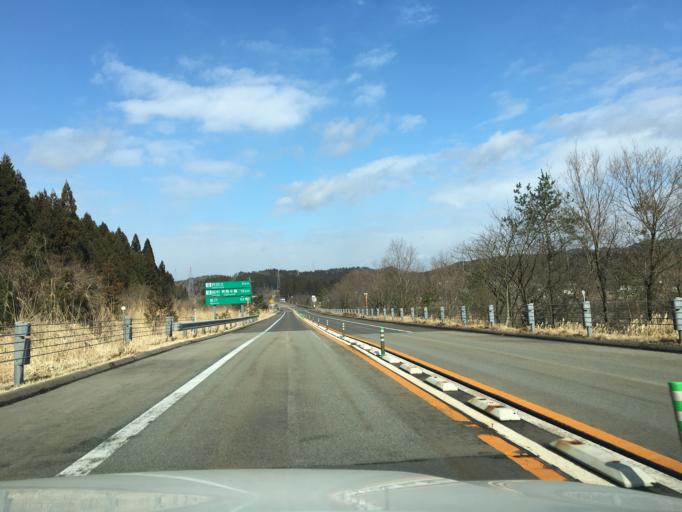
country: JP
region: Akita
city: Akita
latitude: 39.7340
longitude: 140.1760
